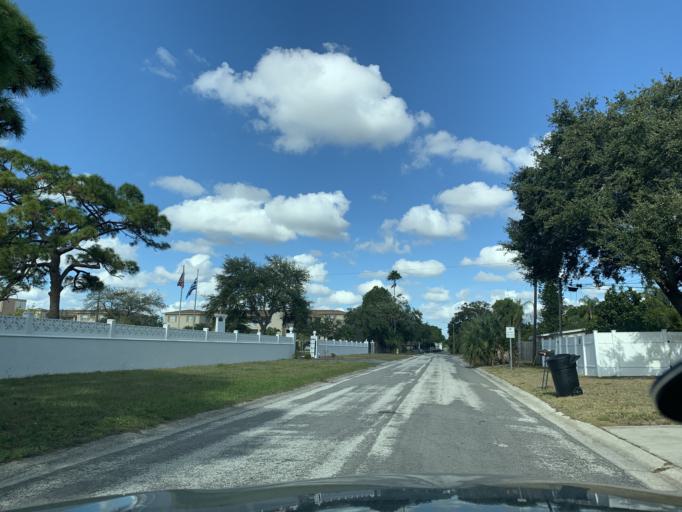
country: US
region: Florida
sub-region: Pinellas County
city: Kenneth City
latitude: 27.8047
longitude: -82.7433
